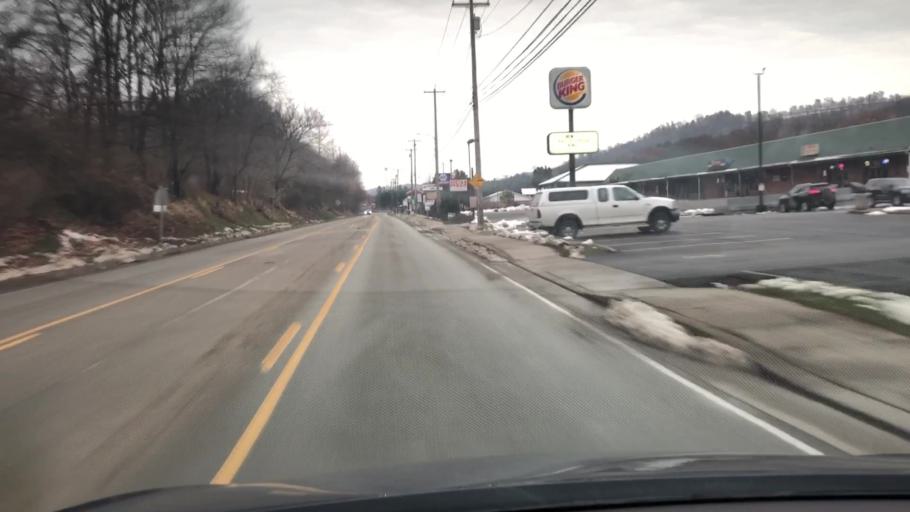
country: US
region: Pennsylvania
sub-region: Clarion County
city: Clarion
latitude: 41.0025
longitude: -79.3250
